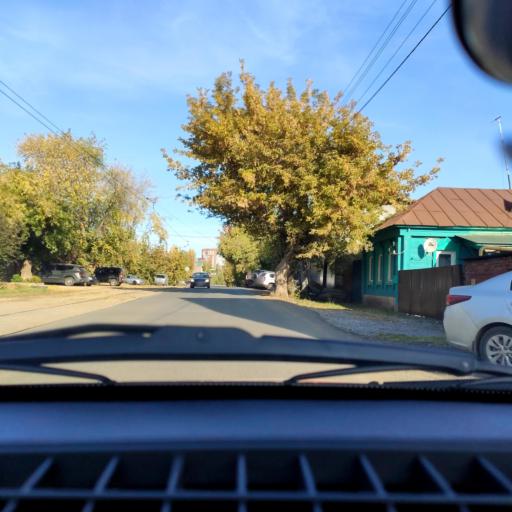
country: RU
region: Bashkortostan
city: Ufa
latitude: 54.7174
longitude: 55.9716
